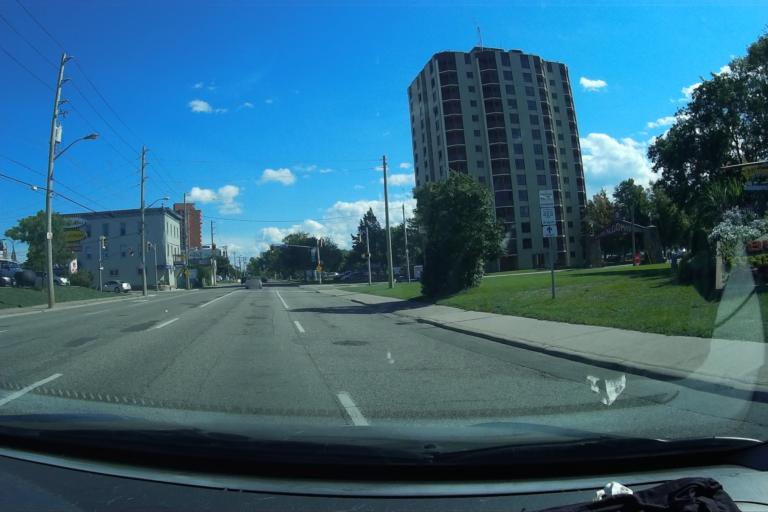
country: CA
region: Ontario
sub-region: Algoma
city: Sault Ste. Marie
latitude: 46.5087
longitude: -84.3318
